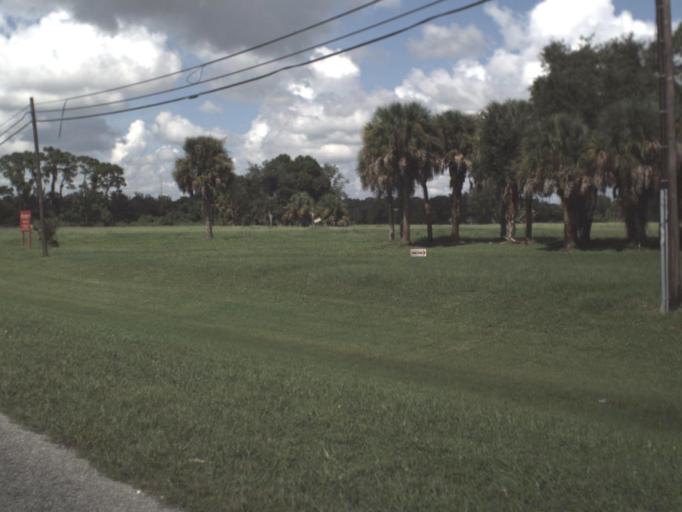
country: US
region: Florida
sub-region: Sarasota County
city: Osprey
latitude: 27.1747
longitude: -82.4798
